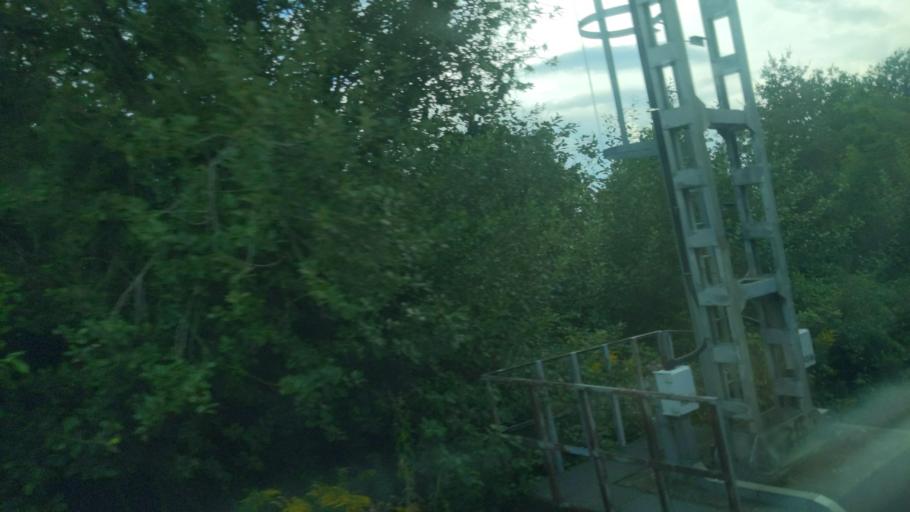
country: CZ
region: Central Bohemia
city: Cesky Brod
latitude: 50.0784
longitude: 14.7999
